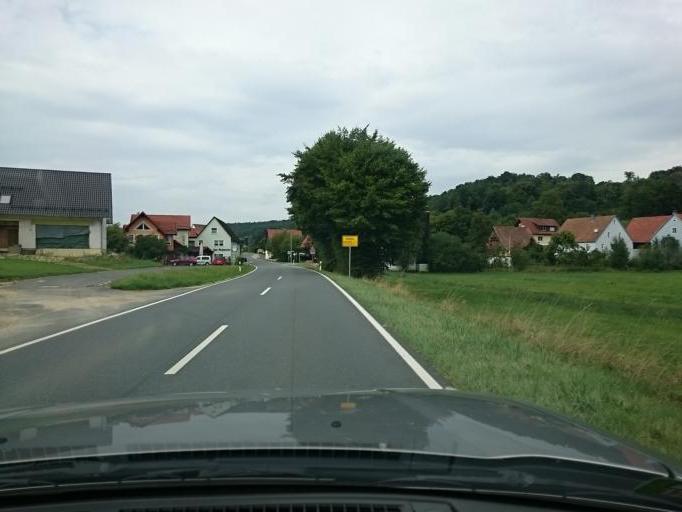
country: DE
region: Bavaria
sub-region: Regierungsbezirk Mittelfranken
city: Velden
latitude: 49.6410
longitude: 11.5133
